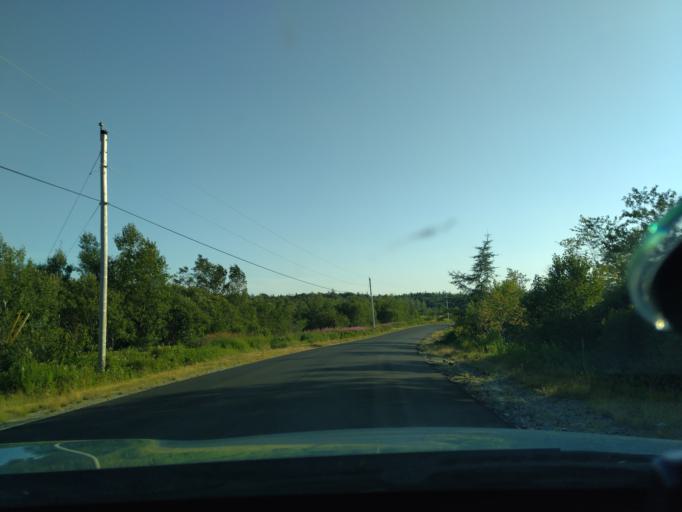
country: US
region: Maine
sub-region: Washington County
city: Machiasport
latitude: 44.6885
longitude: -67.1672
